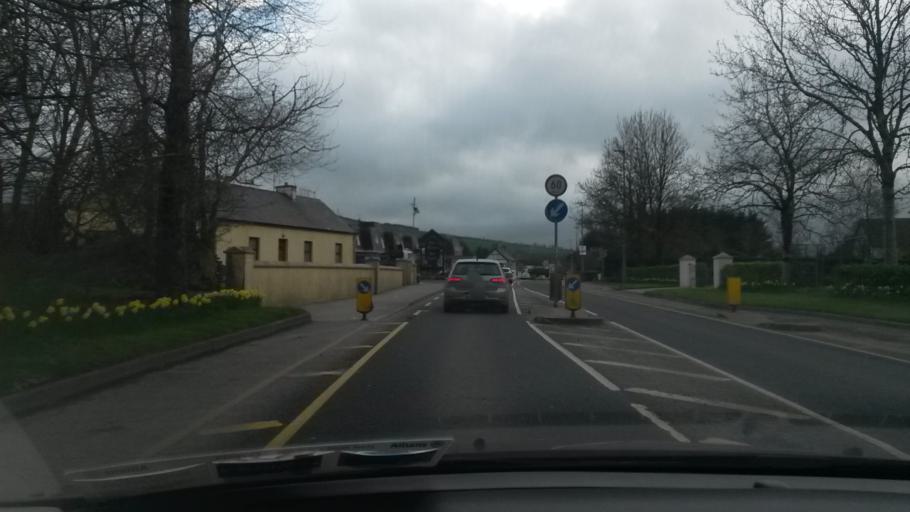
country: IE
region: Munster
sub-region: County Limerick
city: Newcastle West
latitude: 52.3982
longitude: -9.1734
